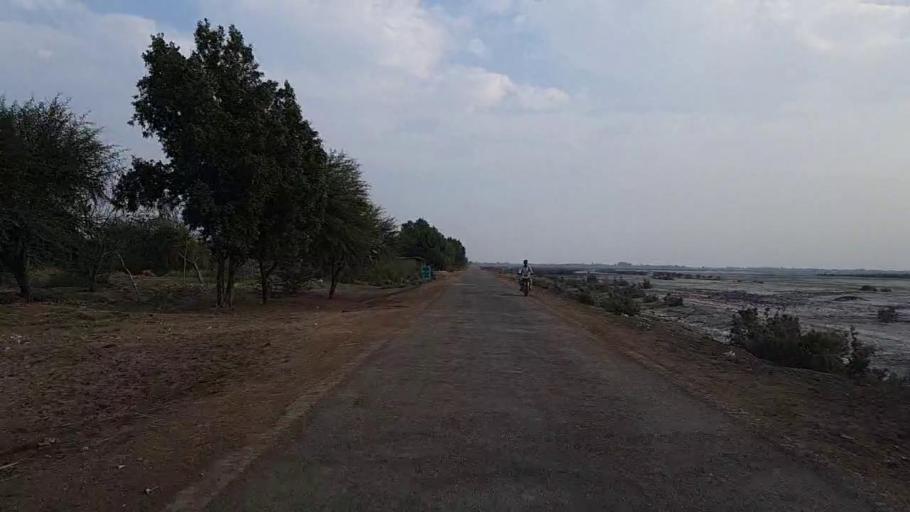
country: PK
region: Sindh
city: Pithoro
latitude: 25.4781
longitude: 69.2666
